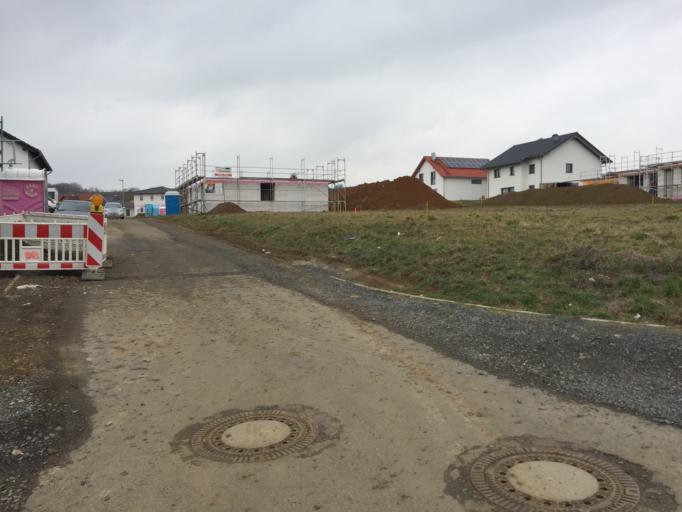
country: DE
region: Hesse
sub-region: Regierungsbezirk Giessen
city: Grunberg
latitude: 50.5790
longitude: 8.9573
